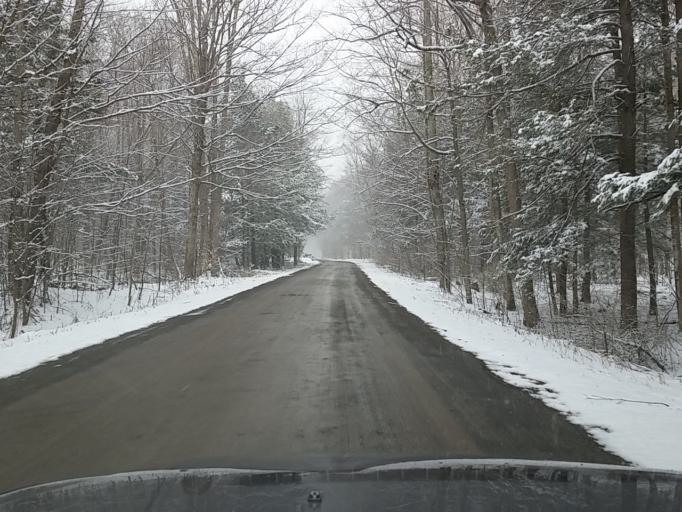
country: US
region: Pennsylvania
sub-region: Sullivan County
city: Laporte
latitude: 41.3219
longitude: -76.4523
